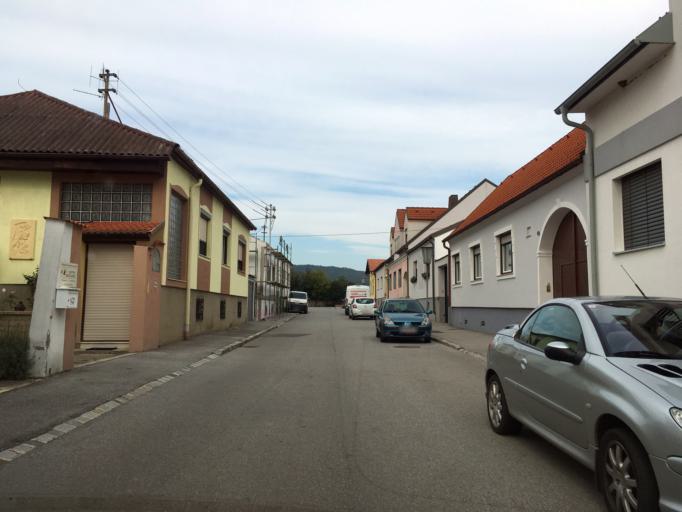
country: AT
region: Burgenland
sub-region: Politischer Bezirk Neusiedl am See
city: Winden am See
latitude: 47.9550
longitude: 16.7520
